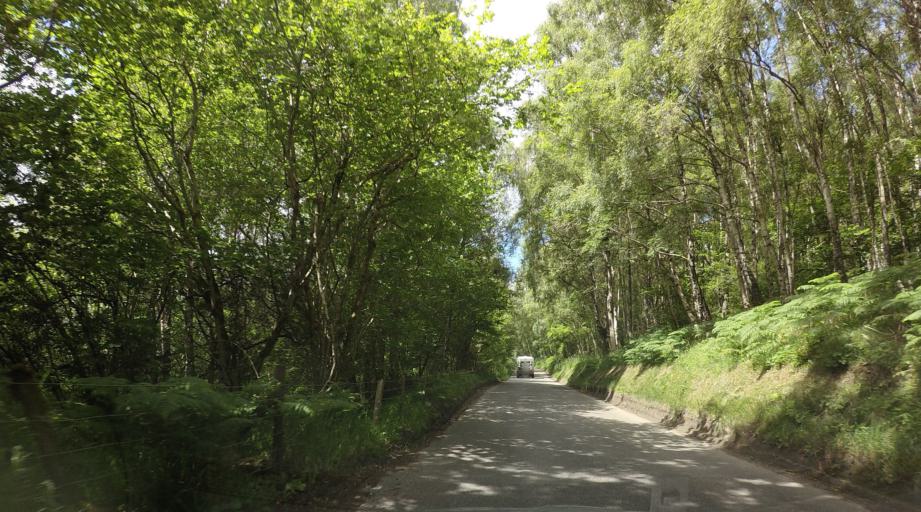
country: GB
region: Scotland
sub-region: Perth and Kinross
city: Aberfeldy
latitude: 56.7170
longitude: -3.9173
